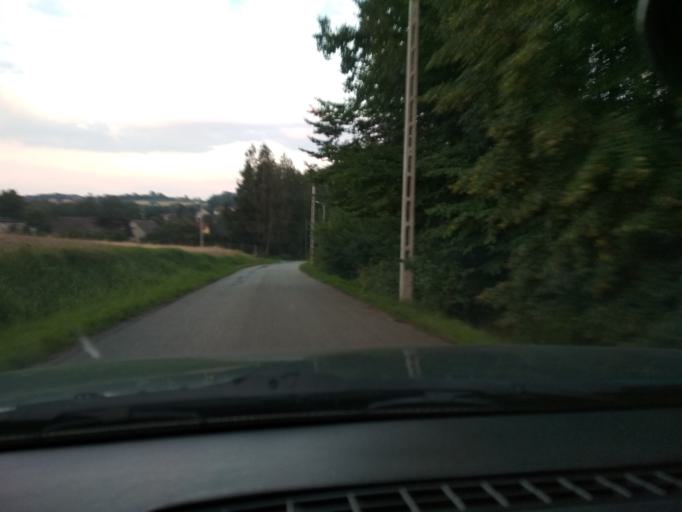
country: PL
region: Silesian Voivodeship
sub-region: Powiat bielski
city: Jasienica
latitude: 49.8389
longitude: 18.9353
